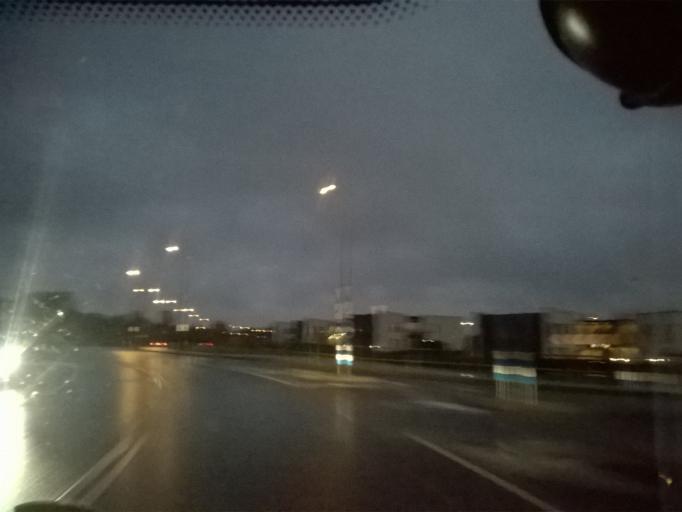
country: EE
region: Harju
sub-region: Viimsi vald
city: Viimsi
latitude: 59.5091
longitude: 24.8551
